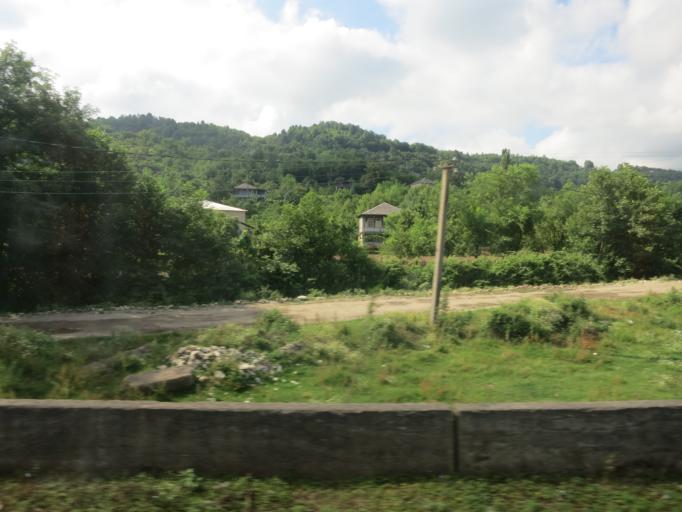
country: GE
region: Imereti
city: Samtredia
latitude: 42.1024
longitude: 42.2809
